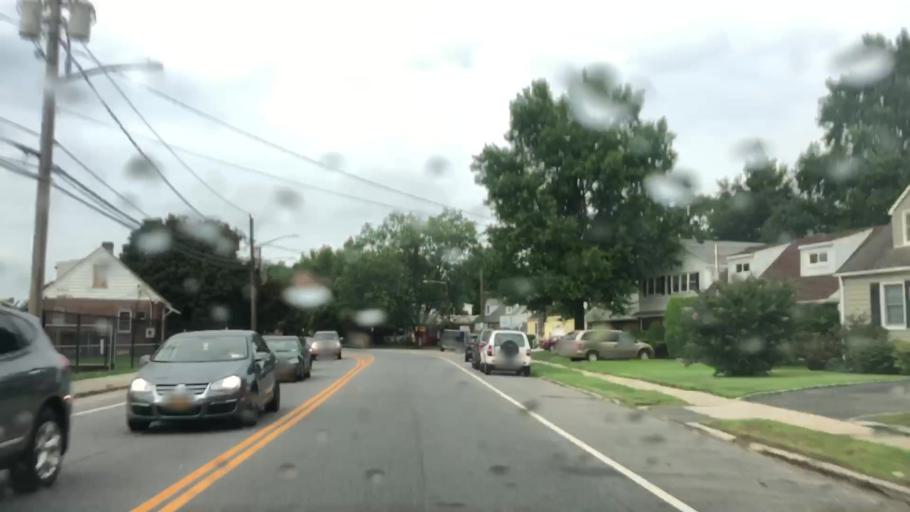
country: US
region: New York
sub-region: Nassau County
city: Stewart Manor
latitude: 40.7146
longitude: -73.6886
